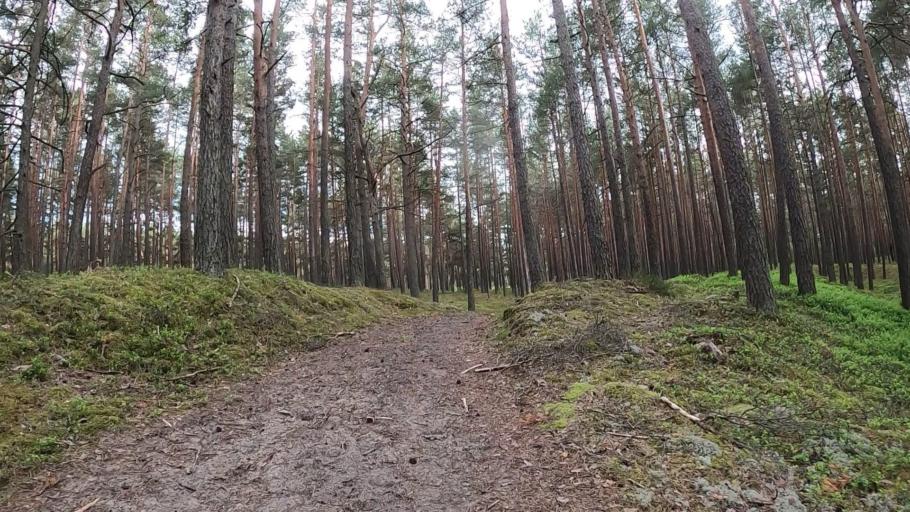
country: LV
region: Riga
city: Jaunciems
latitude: 57.0897
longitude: 24.1629
